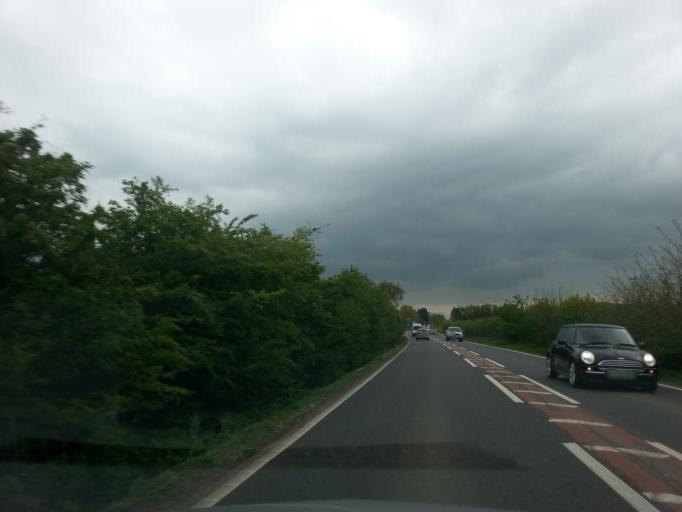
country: GB
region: England
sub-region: Peterborough
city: Wansford
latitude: 52.5842
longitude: -0.4008
